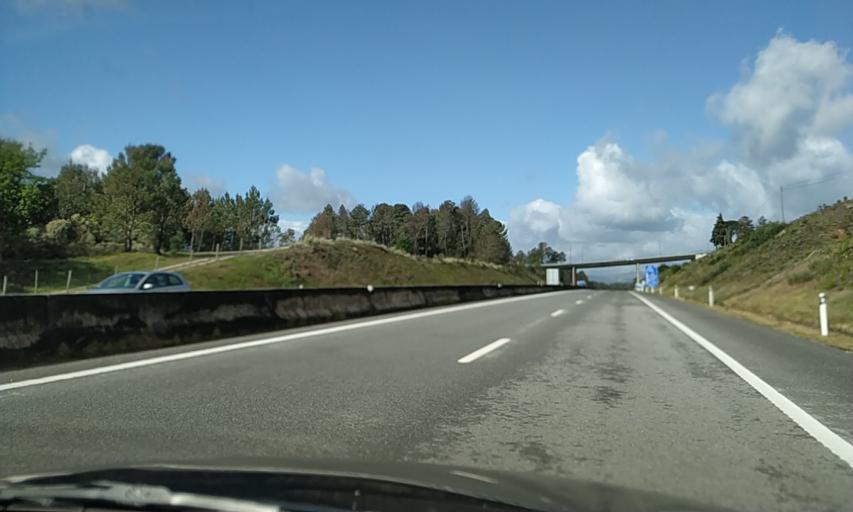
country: PT
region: Viseu
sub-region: Viseu
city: Viseu
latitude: 40.6243
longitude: -7.9391
